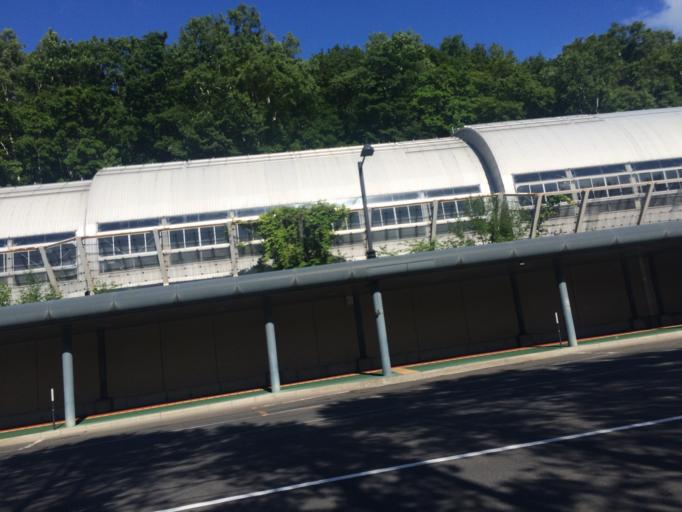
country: JP
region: Hokkaido
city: Sapporo
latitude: 42.9924
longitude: 141.3583
